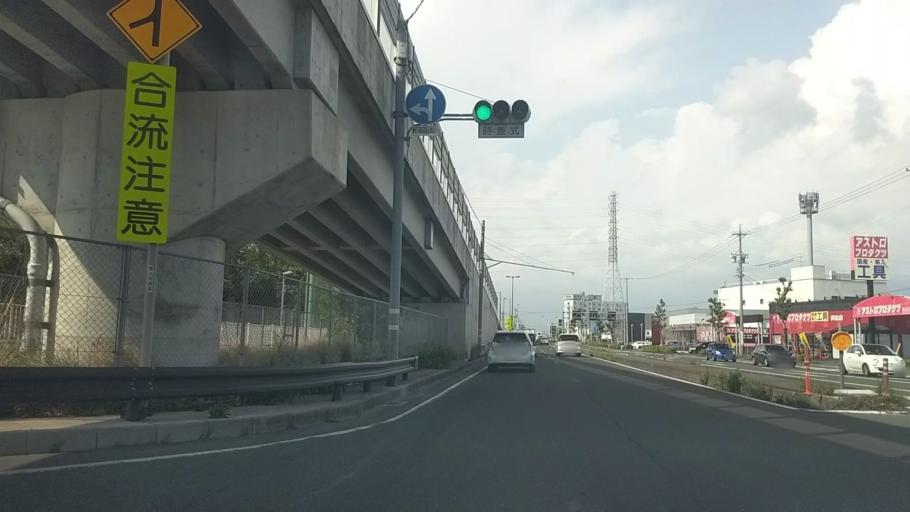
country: JP
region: Shizuoka
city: Hamamatsu
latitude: 34.7303
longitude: 137.7869
